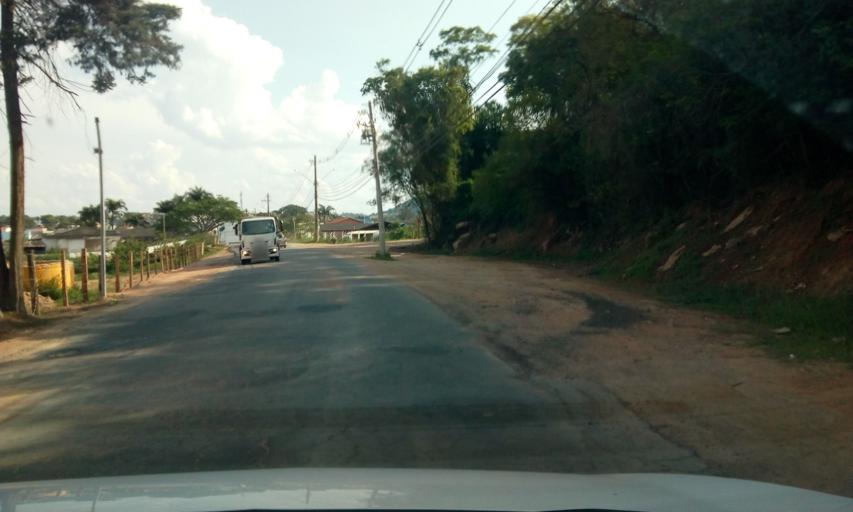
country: BR
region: Sao Paulo
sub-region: Itupeva
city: Itupeva
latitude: -23.1489
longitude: -47.0560
